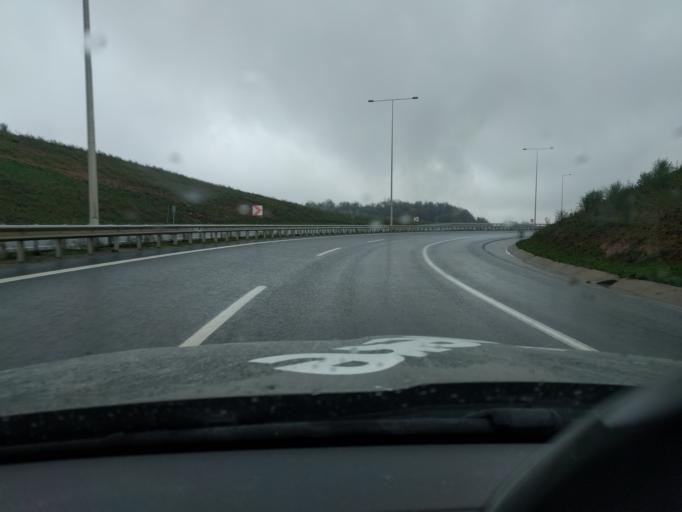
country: TR
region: Istanbul
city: Kemerburgaz
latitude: 41.2127
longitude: 28.8255
